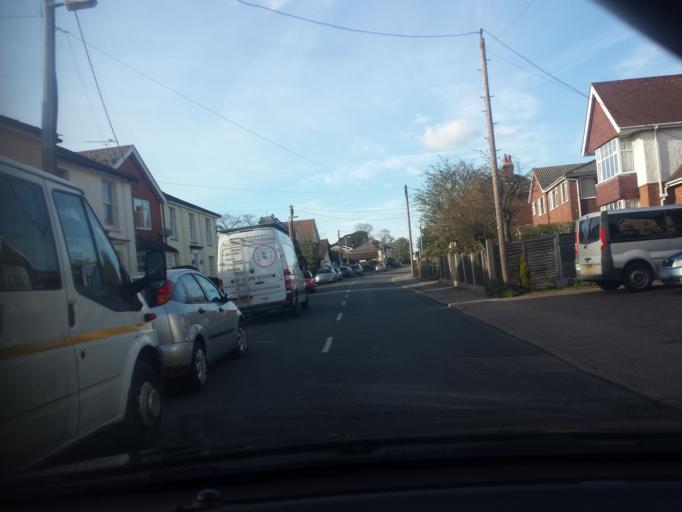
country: GB
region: England
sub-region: Essex
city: Brightlingsea
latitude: 51.8158
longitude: 1.0226
